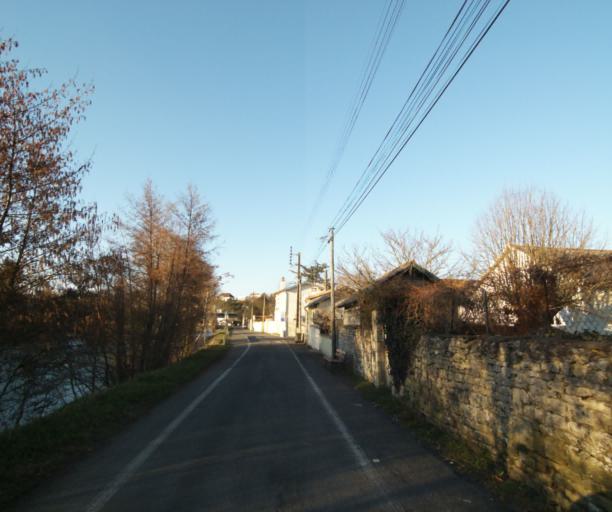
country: FR
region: Poitou-Charentes
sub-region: Departement des Deux-Sevres
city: Niort
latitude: 46.3325
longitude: -0.4786
